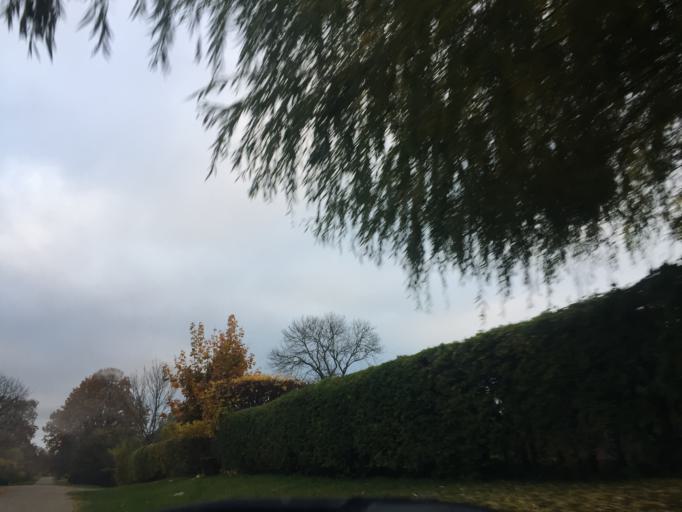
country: LV
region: Skrunda
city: Skrunda
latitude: 56.6769
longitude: 22.0256
